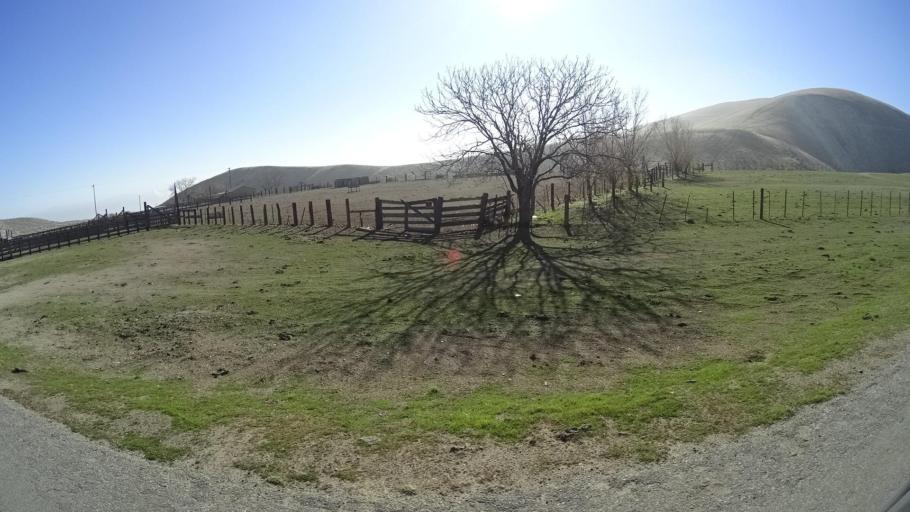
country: US
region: California
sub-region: Kern County
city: Taft Heights
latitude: 35.2331
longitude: -119.6607
